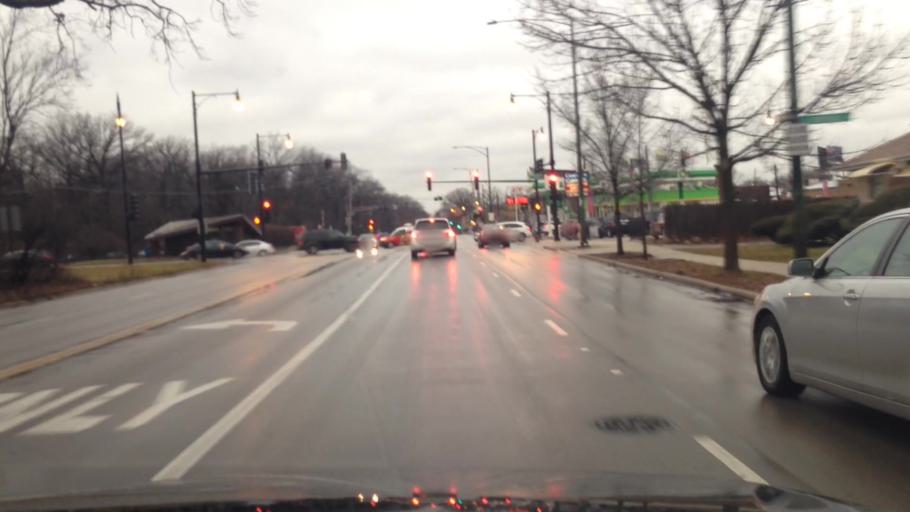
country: US
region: Illinois
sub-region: Cook County
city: Lincolnwood
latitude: 41.9958
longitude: -87.7634
